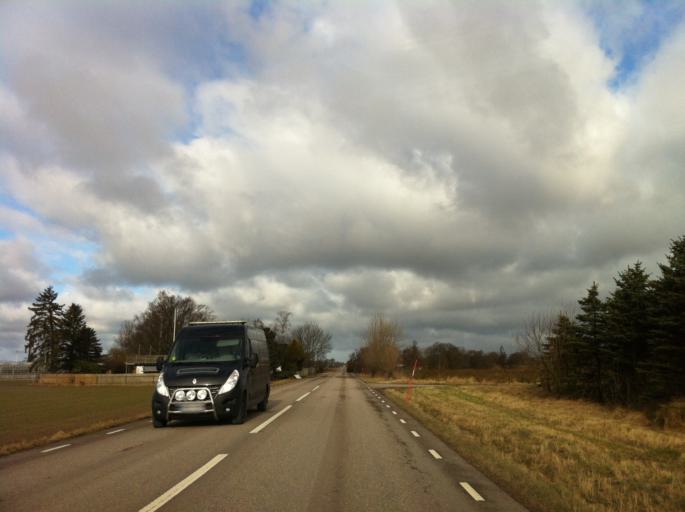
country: SE
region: Skane
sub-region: Helsingborg
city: Hyllinge
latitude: 56.1254
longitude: 12.8828
